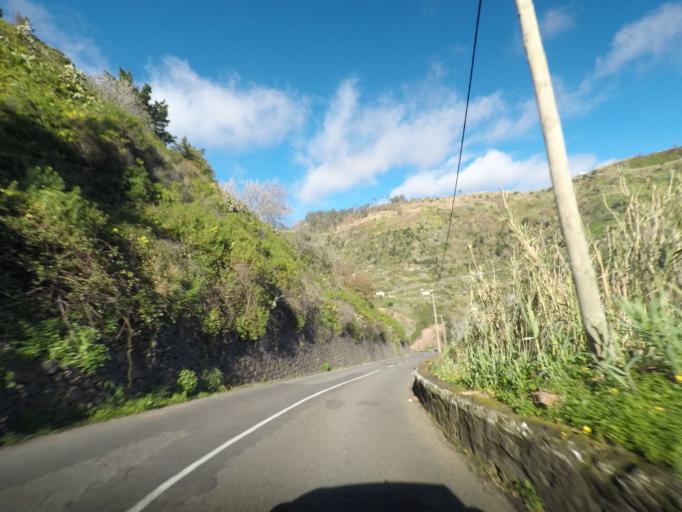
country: PT
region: Madeira
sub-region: Calheta
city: Arco da Calheta
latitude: 32.7103
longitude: -17.1364
